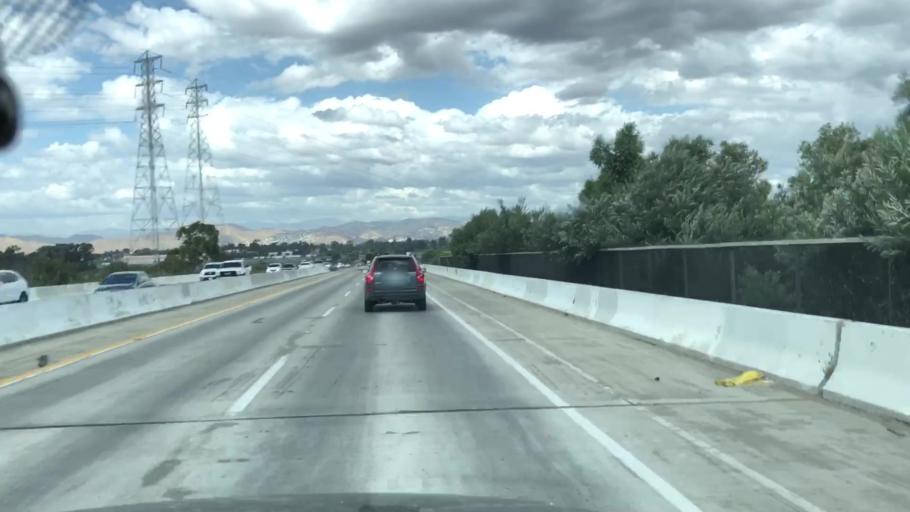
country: US
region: California
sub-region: Ventura County
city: Oxnard Shores
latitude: 34.2360
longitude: -119.2164
